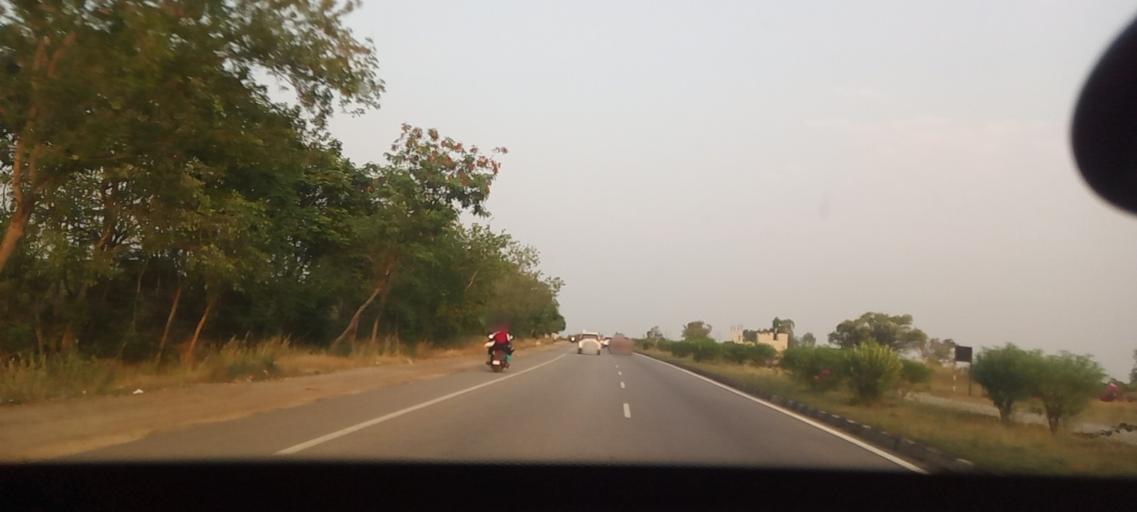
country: IN
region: Karnataka
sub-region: Tumkur
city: Kunigal
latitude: 12.9970
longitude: 76.9200
